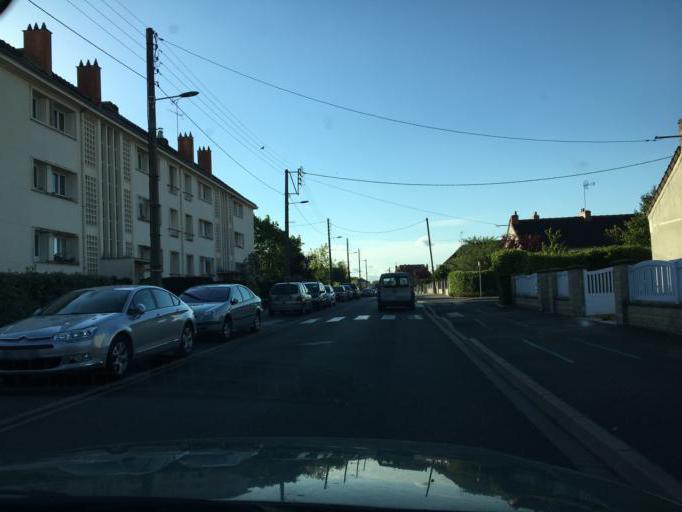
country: FR
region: Centre
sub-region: Departement du Loiret
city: Fleury-les-Aubrais
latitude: 47.9317
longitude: 1.9106
